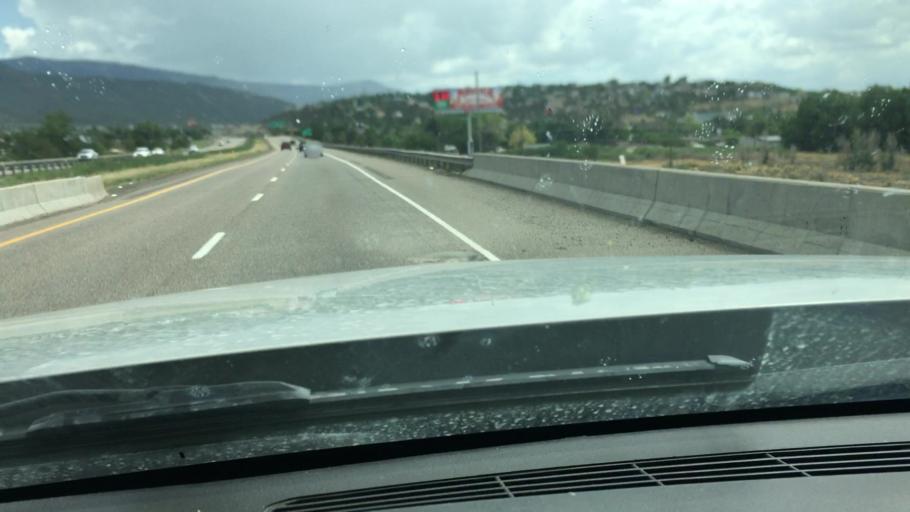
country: US
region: Utah
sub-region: Iron County
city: Cedar City
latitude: 37.6867
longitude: -113.0792
